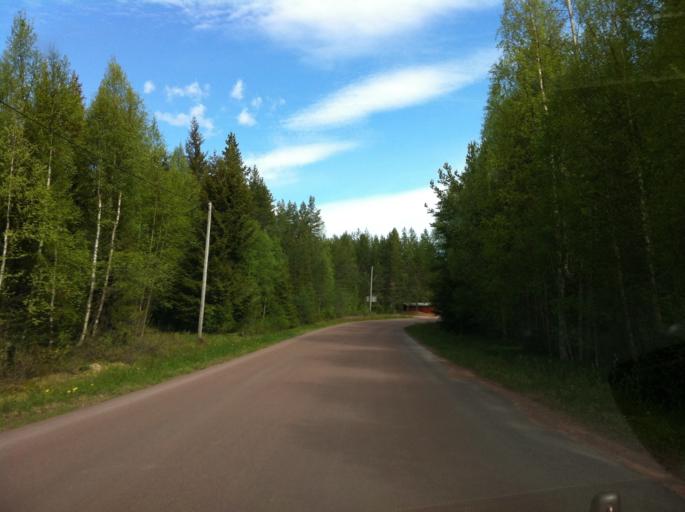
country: SE
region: Dalarna
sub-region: Mora Kommun
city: Mora
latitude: 60.8816
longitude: 14.5174
